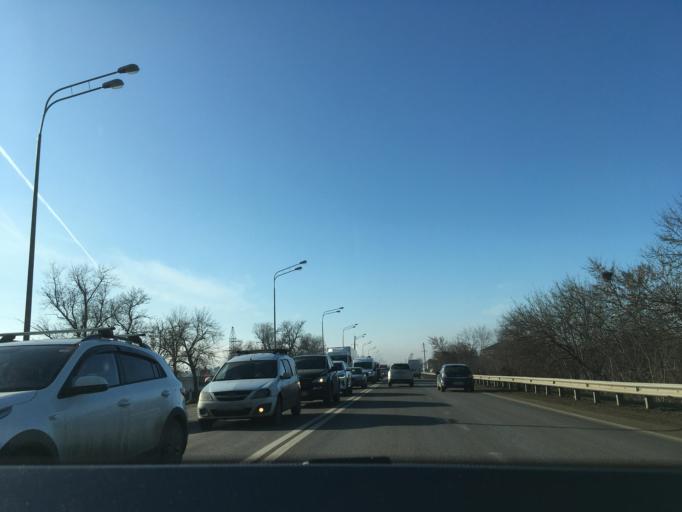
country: RU
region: Krasnodarskiy
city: Krasnodar
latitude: 45.1312
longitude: 39.0199
